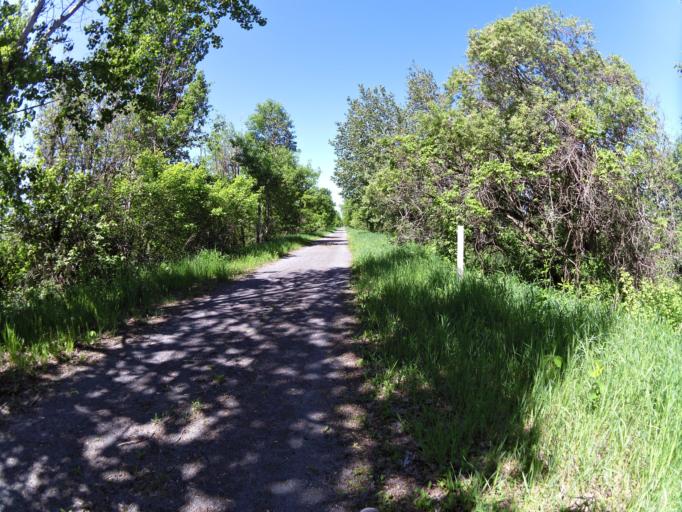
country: CA
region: Ontario
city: Clarence-Rockland
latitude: 45.4263
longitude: -75.3162
